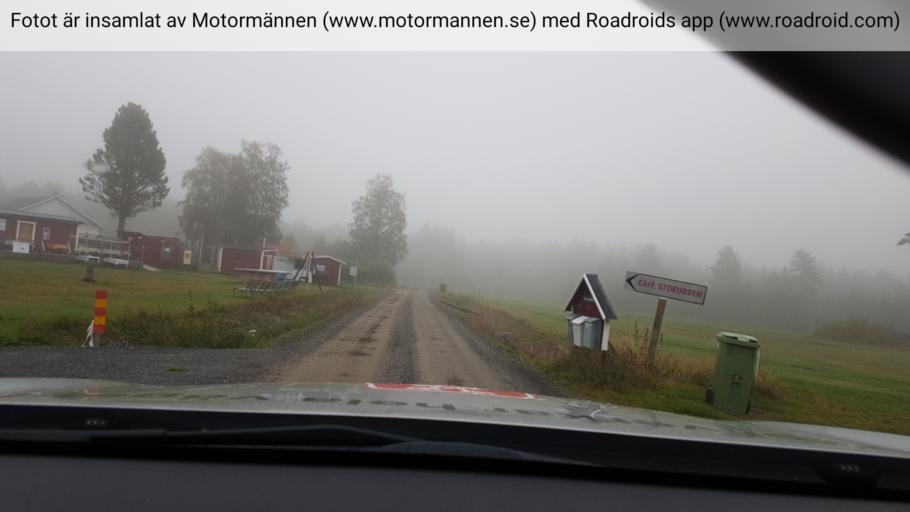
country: SE
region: Vaesterbotten
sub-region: Umea Kommun
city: Ersmark
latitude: 64.1487
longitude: 20.3868
